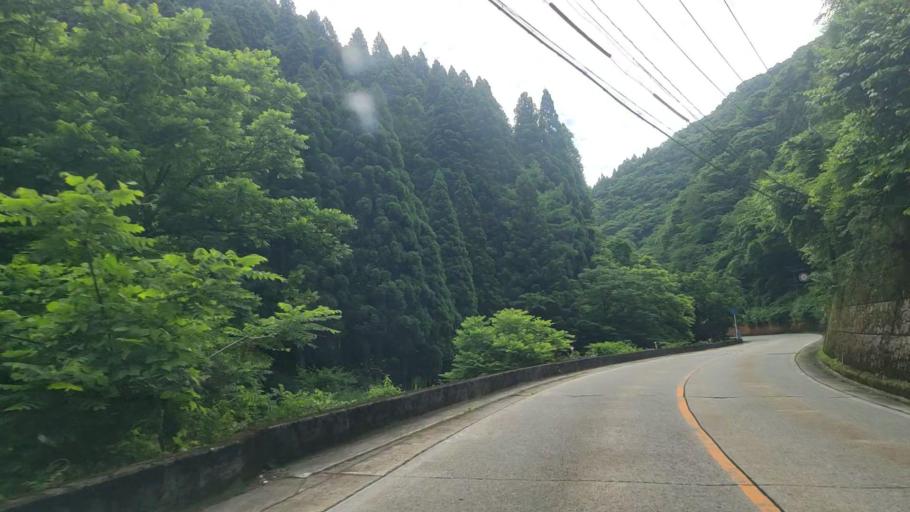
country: JP
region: Okayama
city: Niimi
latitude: 35.2131
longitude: 133.4763
